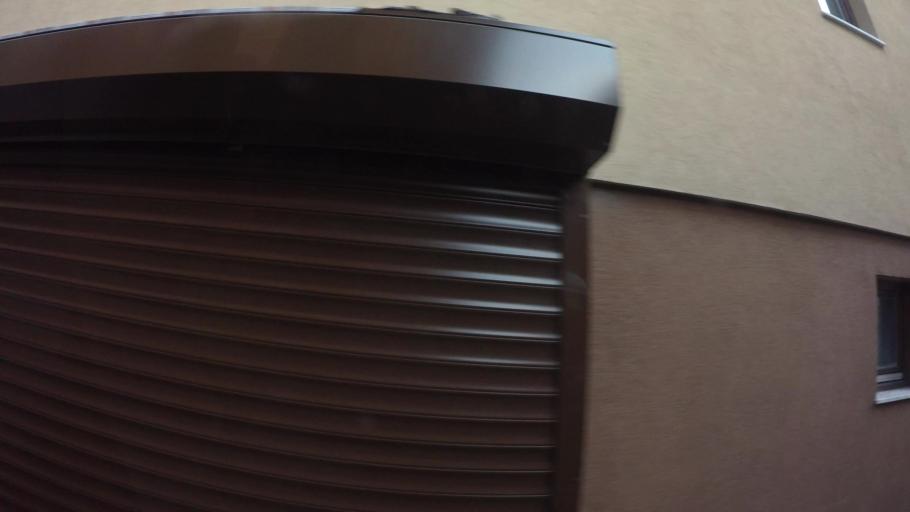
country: BA
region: Federation of Bosnia and Herzegovina
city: Kobilja Glava
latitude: 43.8649
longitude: 18.4364
